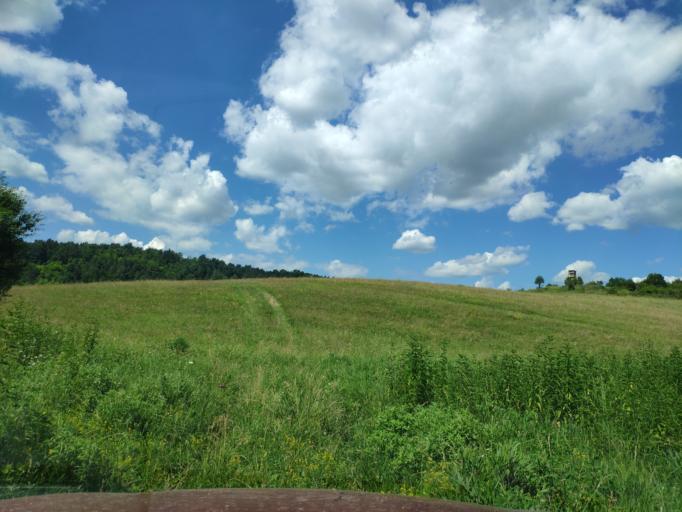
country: HU
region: Borsod-Abauj-Zemplen
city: Arlo
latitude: 48.2610
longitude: 20.1722
